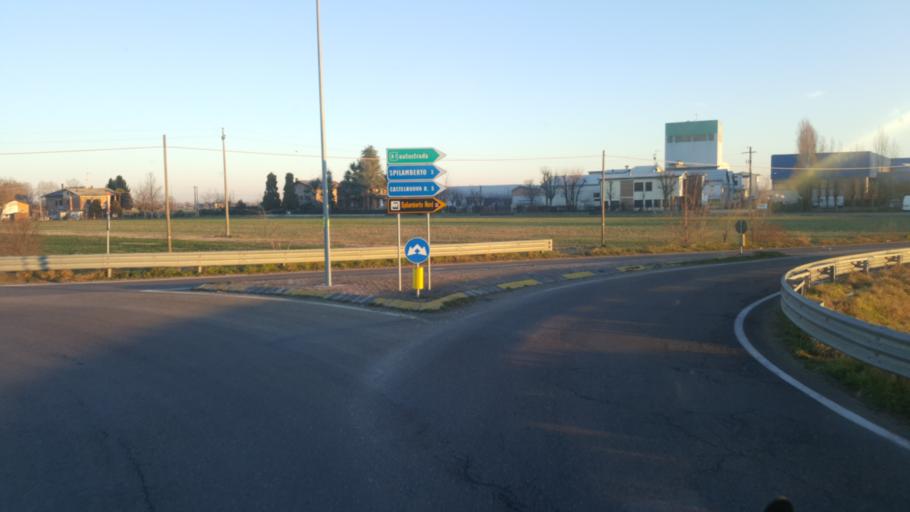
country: IT
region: Emilia-Romagna
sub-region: Provincia di Modena
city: Ca' di Sola
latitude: 44.5291
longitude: 10.9767
